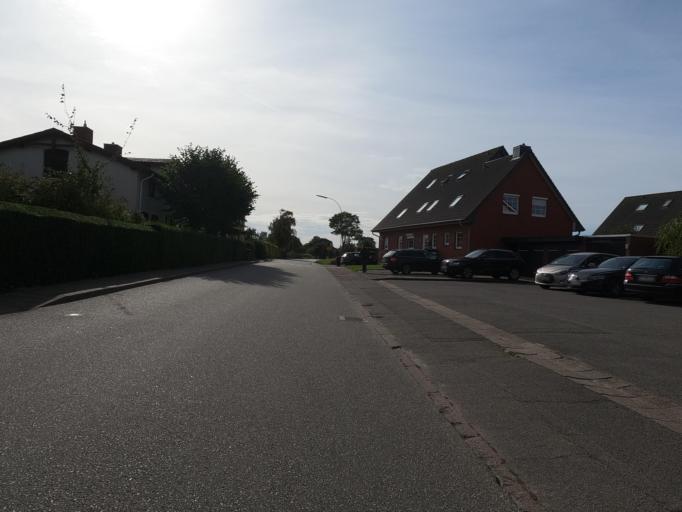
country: DE
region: Schleswig-Holstein
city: Dahme
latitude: 54.2166
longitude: 11.0896
